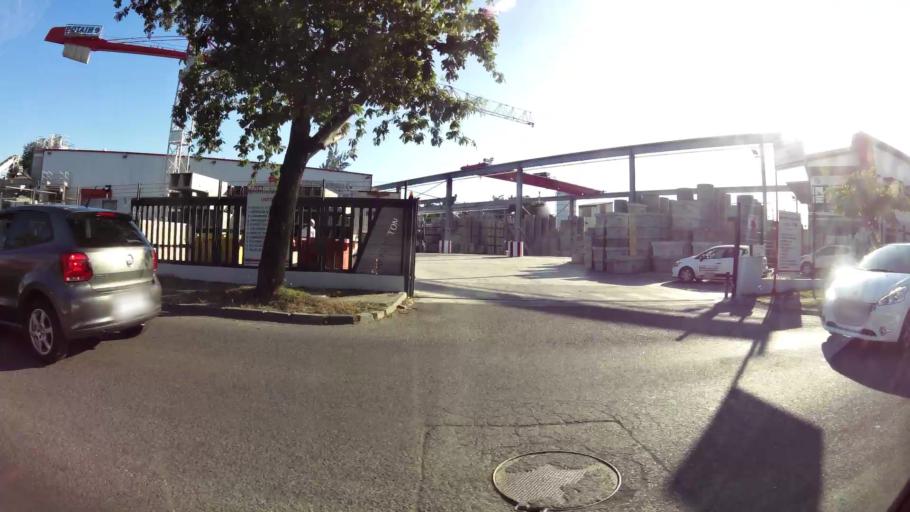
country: RE
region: Reunion
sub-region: Reunion
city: Saint-Louis
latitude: -21.2777
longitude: 55.3734
